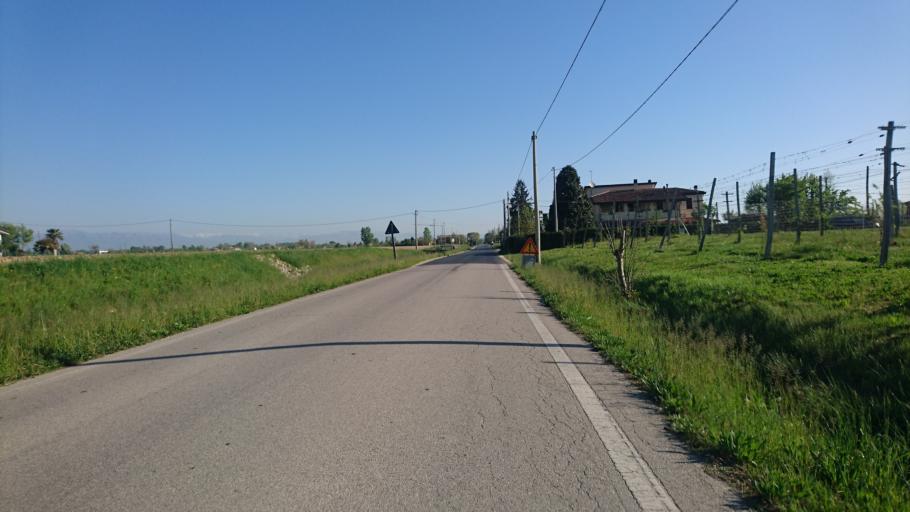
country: IT
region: Veneto
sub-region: Provincia di Venezia
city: Sant'Angelo
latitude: 45.5278
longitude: 12.0011
